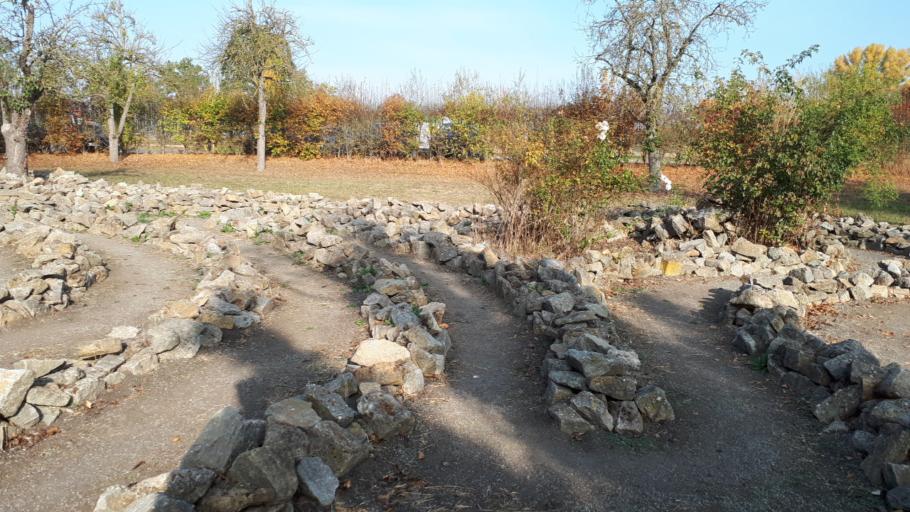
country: DE
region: Bavaria
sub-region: Regierungsbezirk Unterfranken
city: Sommerach
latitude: 49.8061
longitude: 10.2354
